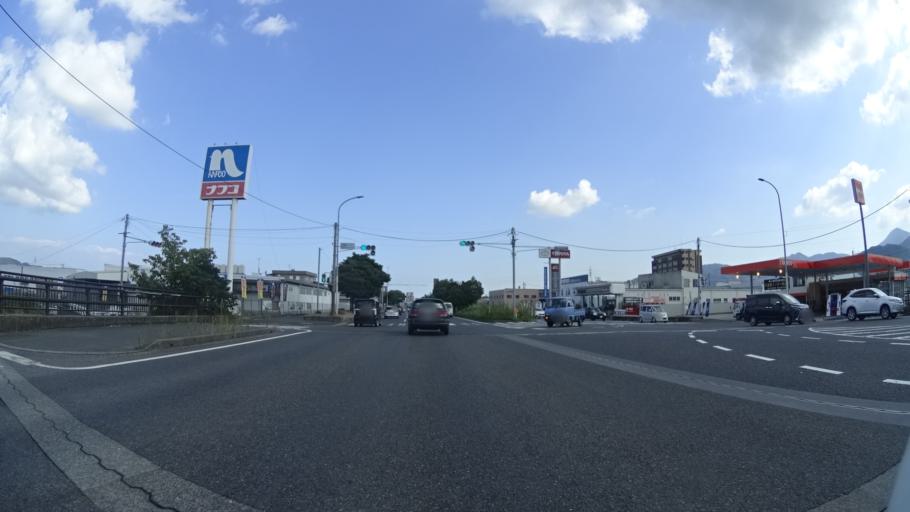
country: JP
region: Fukuoka
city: Kanda
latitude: 33.8333
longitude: 130.9181
